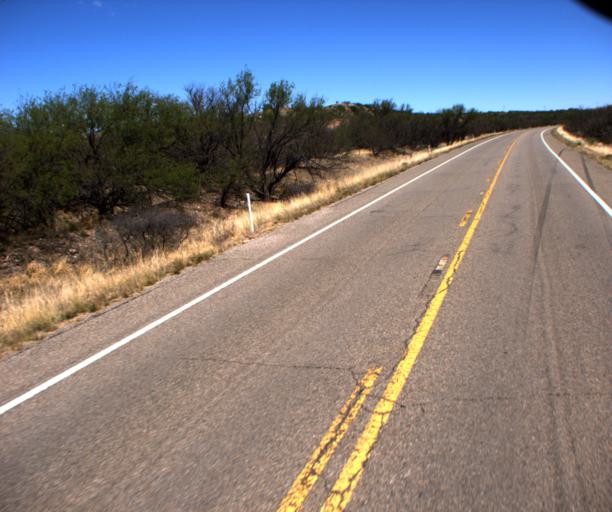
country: US
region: Arizona
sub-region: Santa Cruz County
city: Rio Rico
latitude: 31.6159
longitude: -110.7199
